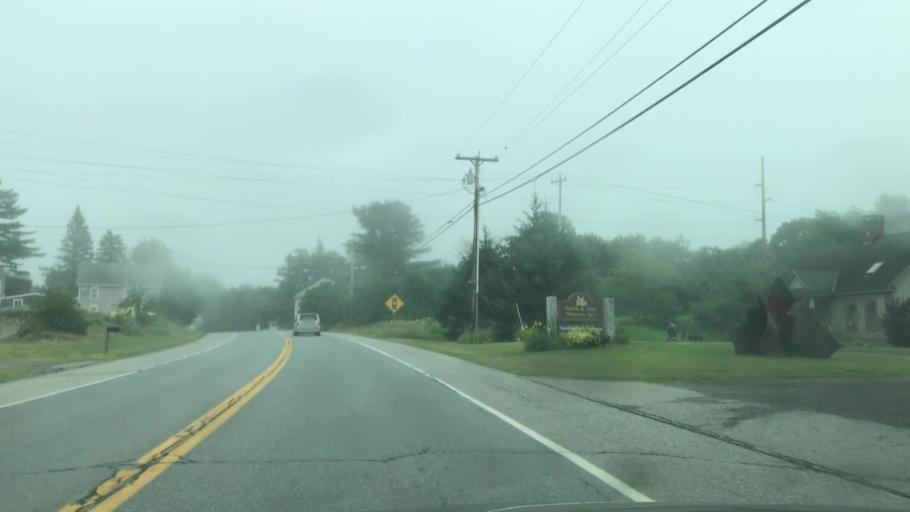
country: US
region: Maine
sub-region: Knox County
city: Rockport
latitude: 44.1801
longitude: -69.1391
